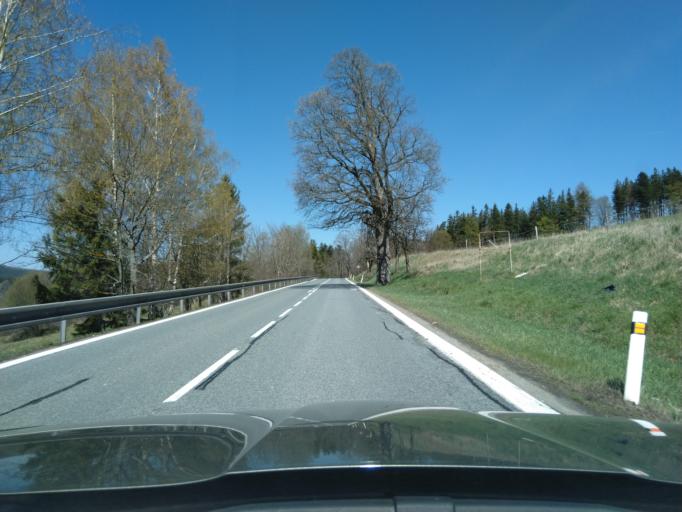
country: CZ
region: Jihocesky
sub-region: Okres Prachatice
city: Vimperk
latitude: 49.0336
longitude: 13.7623
